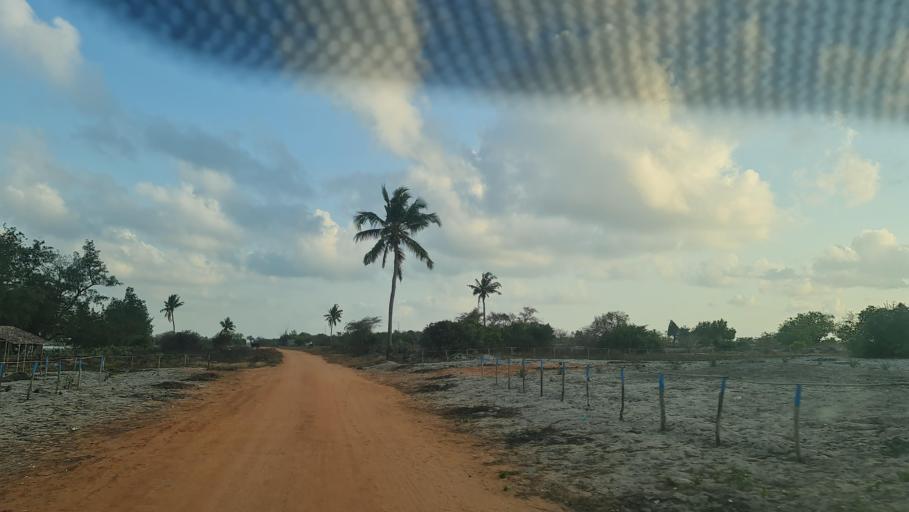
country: MZ
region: Nampula
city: Nacala
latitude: -14.7853
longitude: 40.8209
